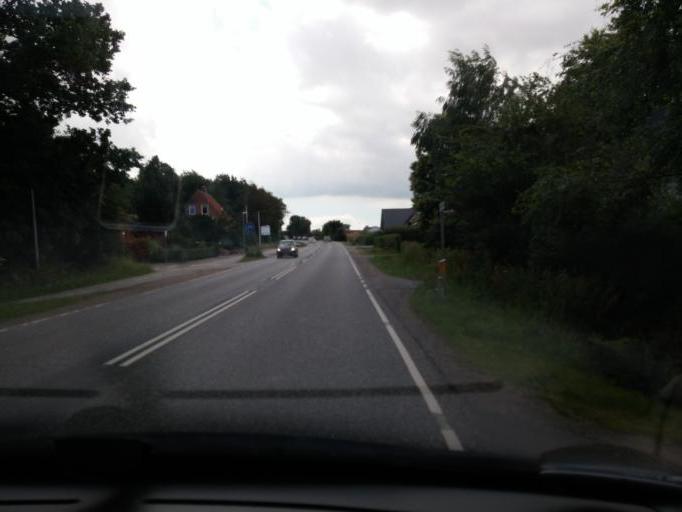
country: DK
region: South Denmark
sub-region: Svendborg Kommune
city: Vindeby
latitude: 55.0285
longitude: 10.6096
